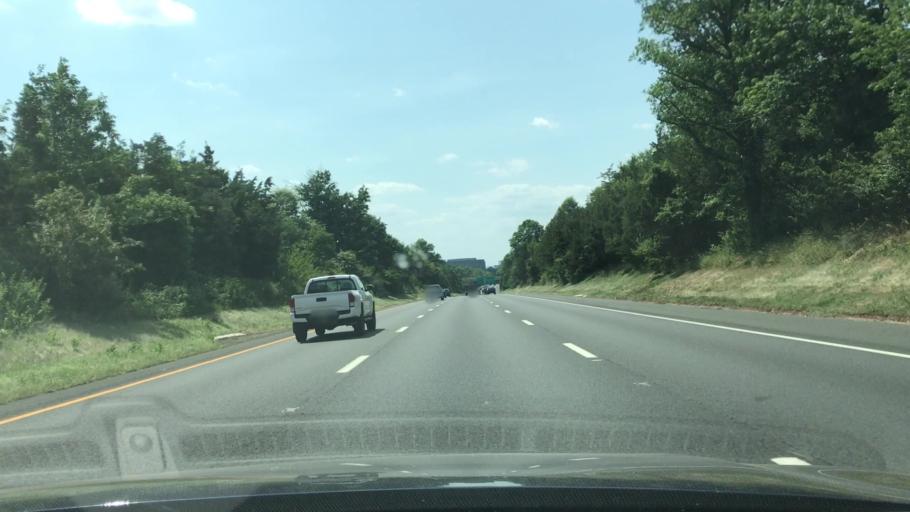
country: US
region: New Jersey
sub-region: Somerset County
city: Somerville
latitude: 40.5812
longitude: -74.5916
